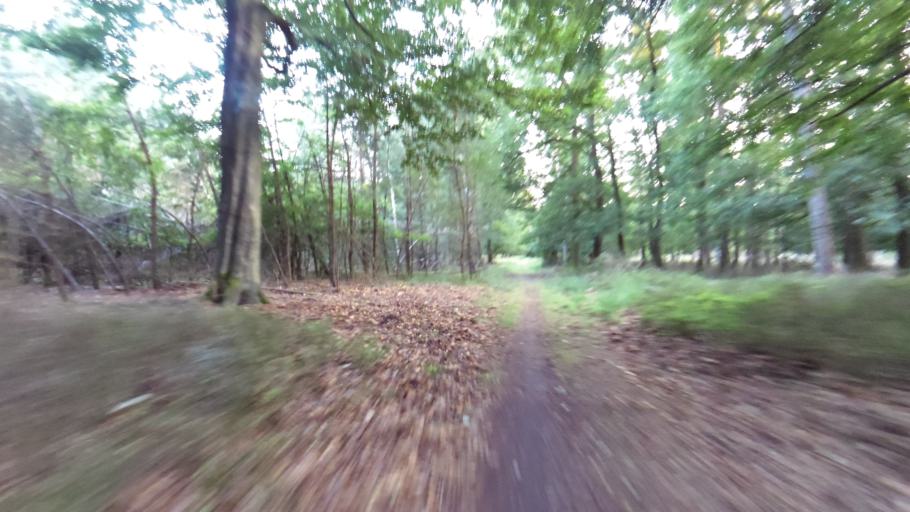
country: NL
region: Gelderland
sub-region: Gemeente Apeldoorn
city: Uddel
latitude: 52.2499
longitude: 5.8659
